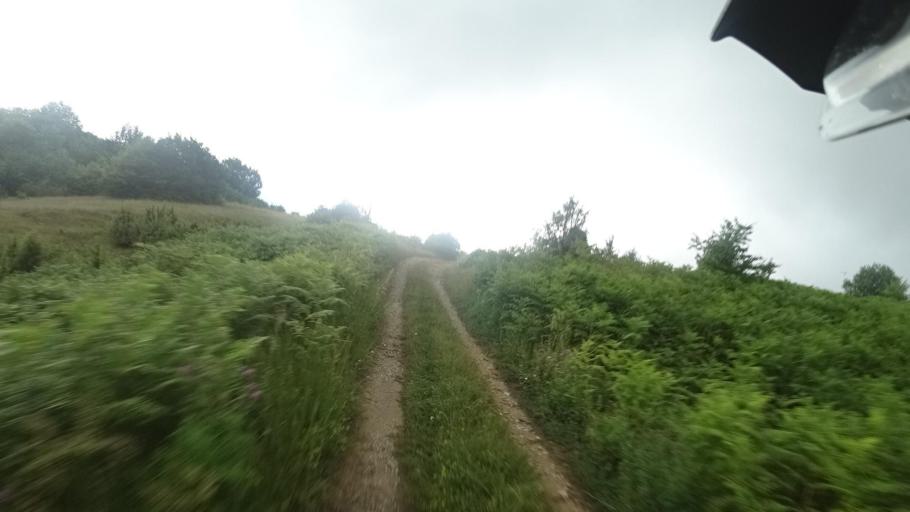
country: HR
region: Licko-Senjska
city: Jezerce
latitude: 44.8158
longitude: 15.6275
